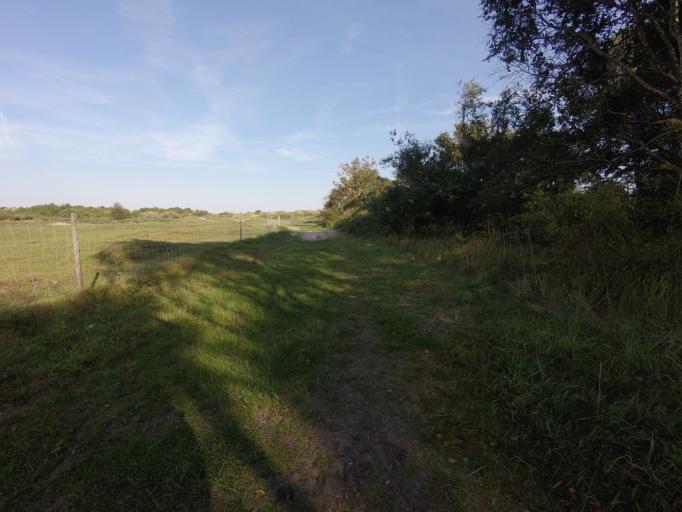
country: NL
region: Friesland
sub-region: Gemeente Schiermonnikoog
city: Schiermonnikoog
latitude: 53.4890
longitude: 6.1787
